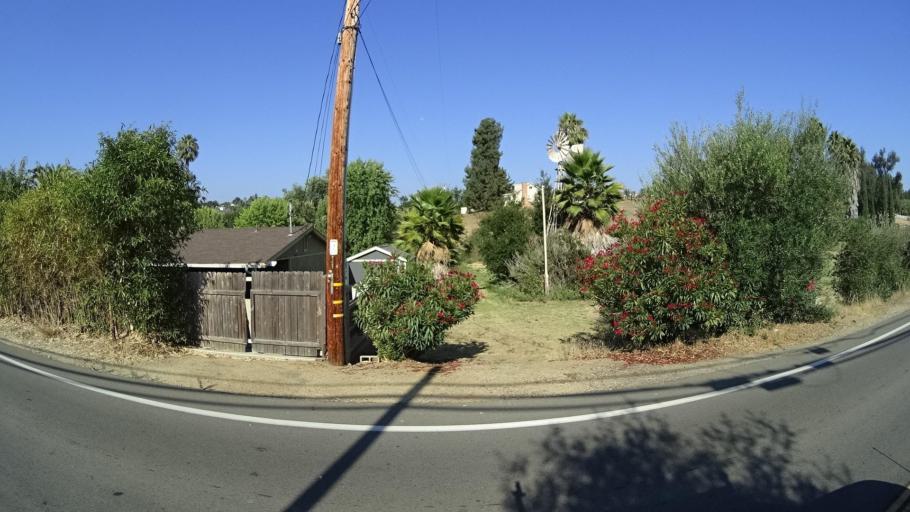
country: US
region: California
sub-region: San Diego County
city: Fallbrook
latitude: 33.3316
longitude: -117.2449
